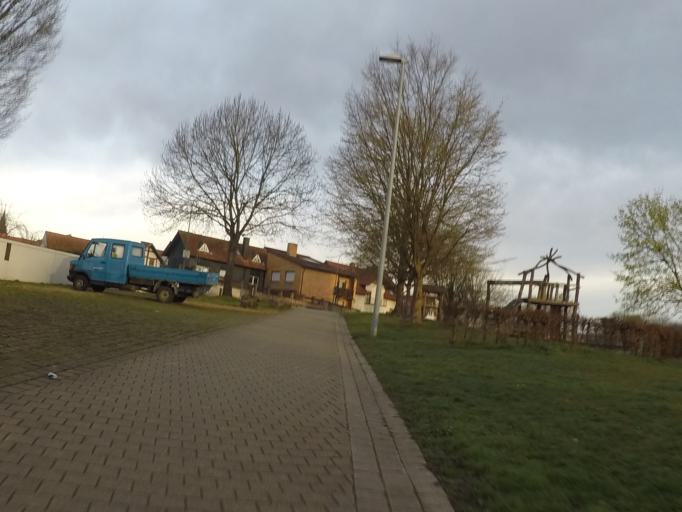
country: DE
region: Rheinland-Pfalz
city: Worth am Rhein
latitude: 49.0512
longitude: 8.2713
